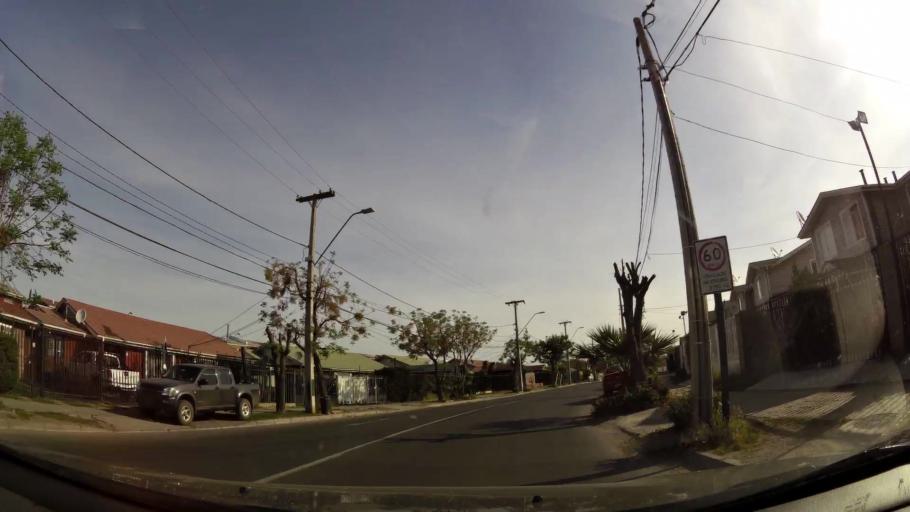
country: CL
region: Santiago Metropolitan
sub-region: Provincia de Cordillera
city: Puente Alto
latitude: -33.5917
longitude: -70.5560
